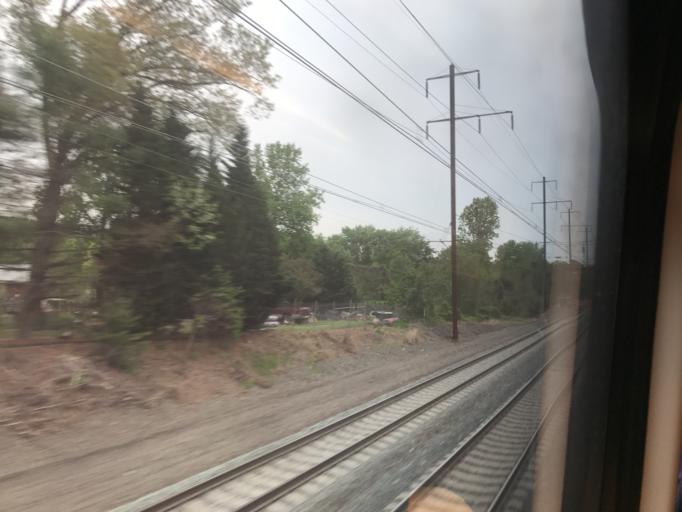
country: US
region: Maryland
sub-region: Prince George's County
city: Glenn Dale
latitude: 39.0035
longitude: -76.7861
